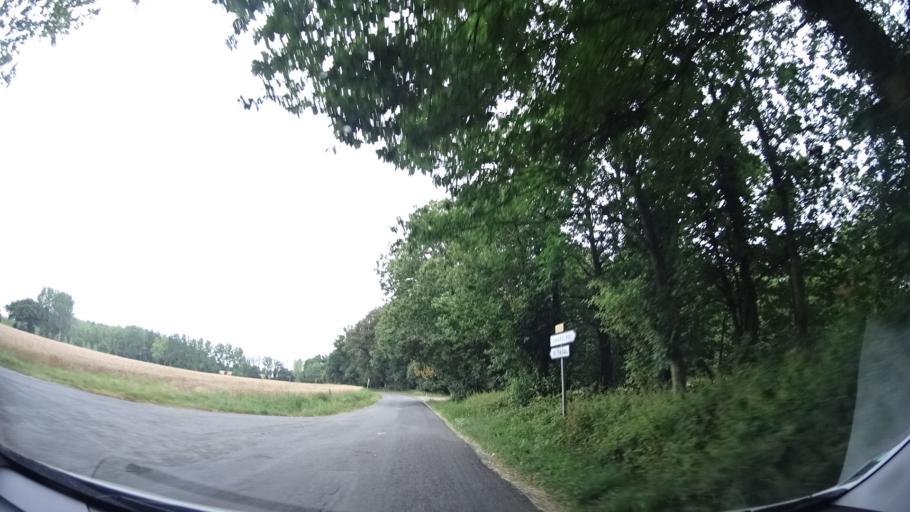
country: FR
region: Brittany
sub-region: Departement d'Ille-et-Vilaine
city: Saint-Domineuc
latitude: 48.3273
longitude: -1.9311
